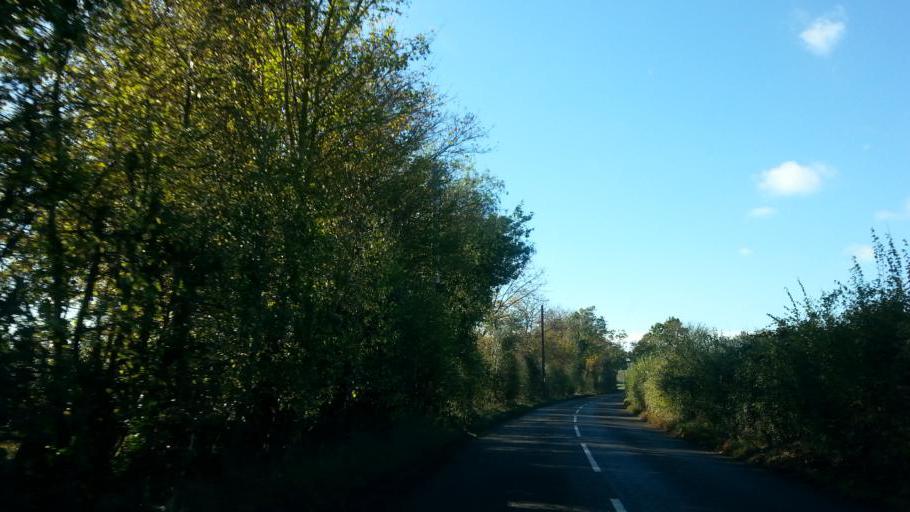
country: GB
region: England
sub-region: Suffolk
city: Cookley
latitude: 52.2922
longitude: 1.3902
